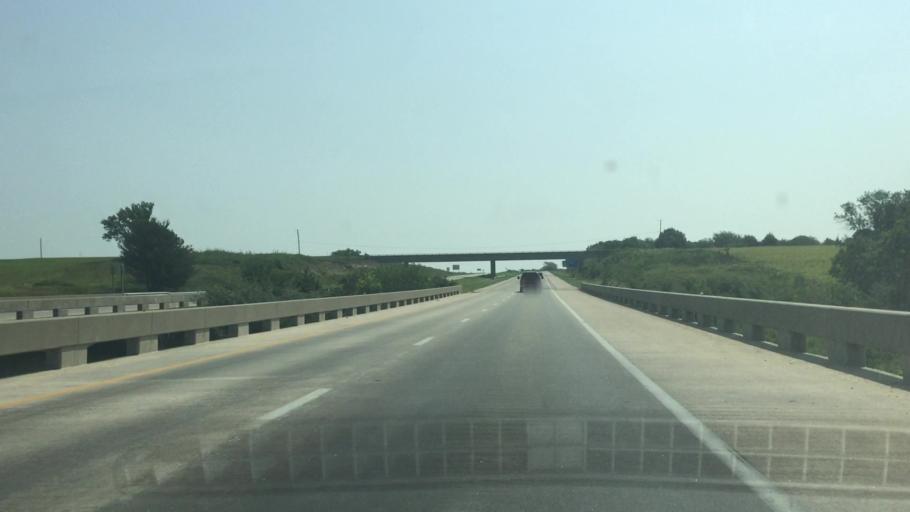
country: US
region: Kansas
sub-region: Osage County
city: Lyndon
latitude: 38.4261
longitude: -95.7508
